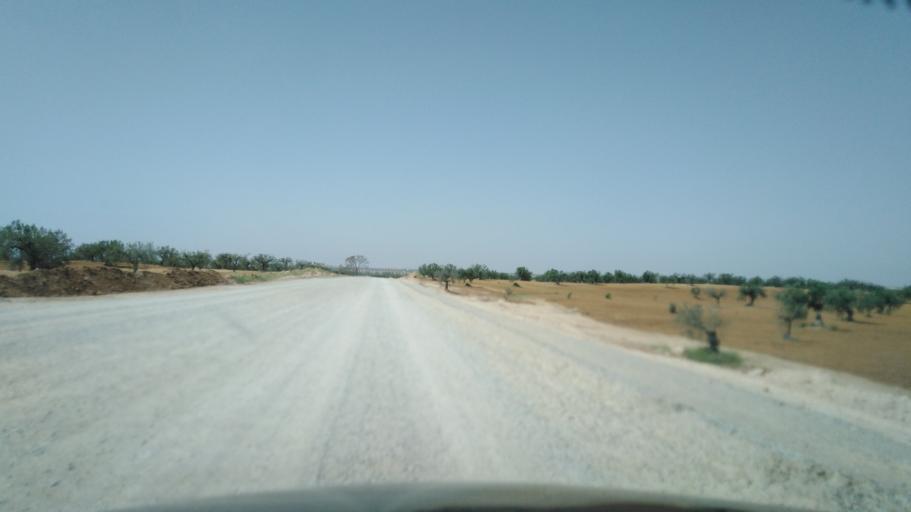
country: TN
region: Safaqis
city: Sfax
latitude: 34.7073
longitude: 10.4938
